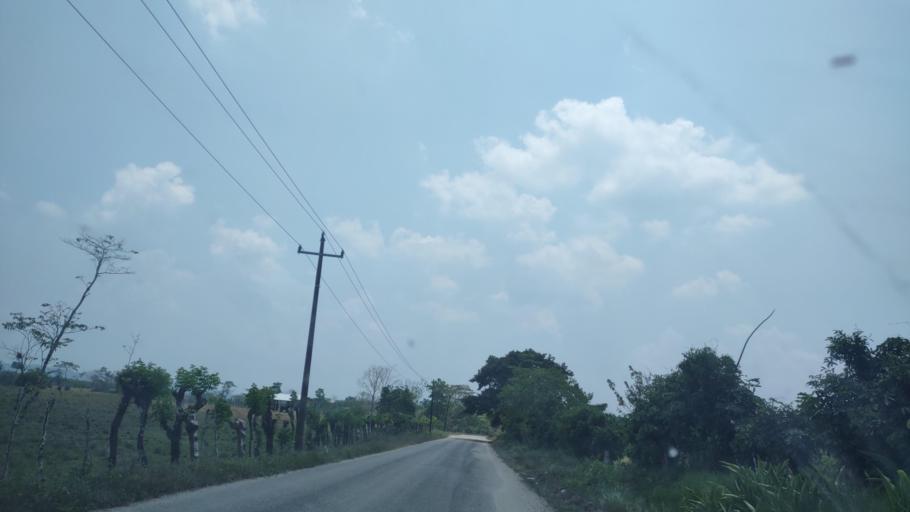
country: MX
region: Tabasco
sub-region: Huimanguillo
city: Francisco Rueda
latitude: 17.6080
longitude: -94.0923
